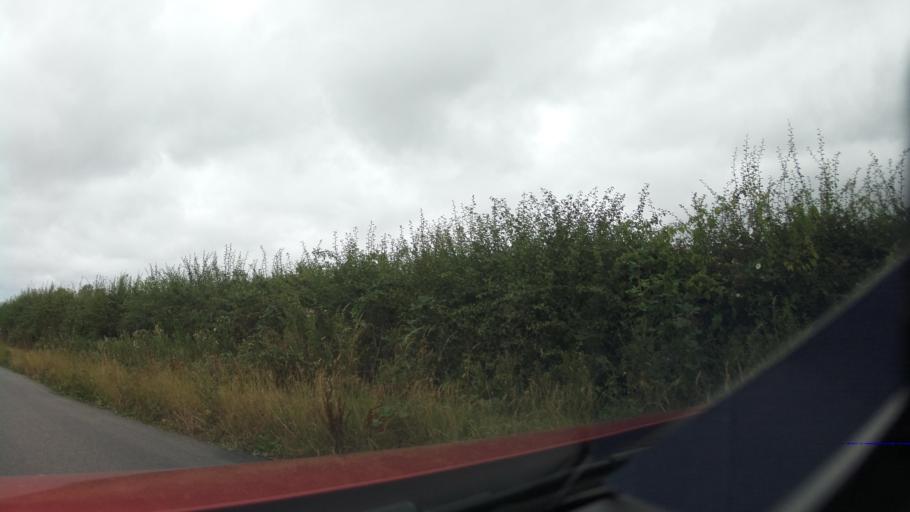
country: GB
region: England
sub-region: Derbyshire
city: Findern
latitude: 52.8761
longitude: -1.5406
